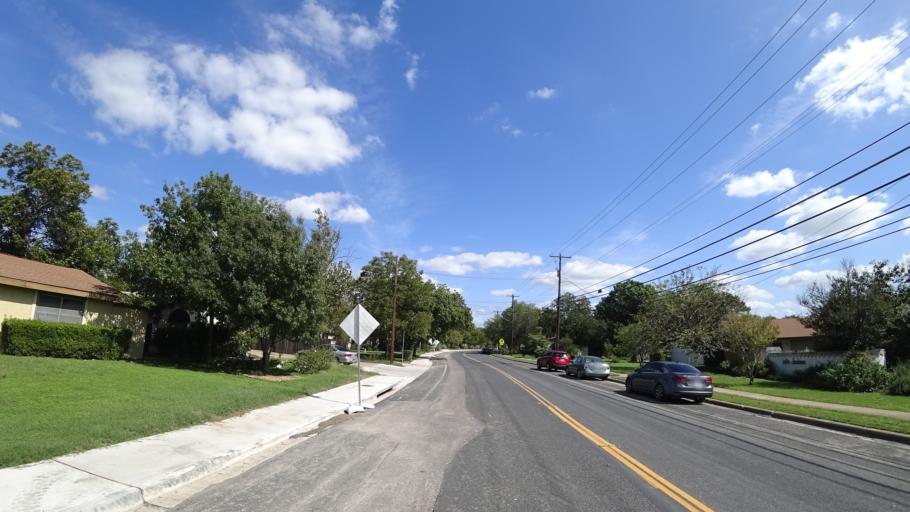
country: US
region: Texas
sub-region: Travis County
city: Austin
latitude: 30.3437
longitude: -97.7335
